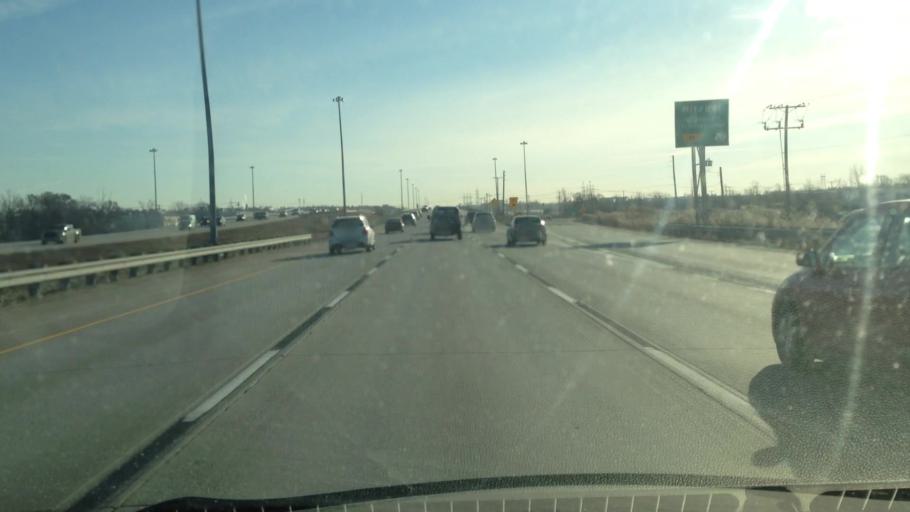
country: CA
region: Quebec
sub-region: Laurentides
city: Blainville
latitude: 45.6952
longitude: -73.9416
